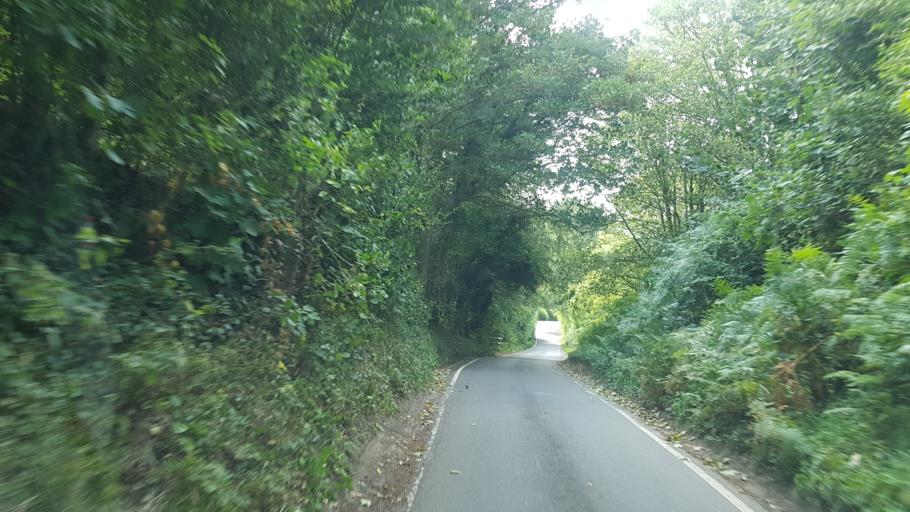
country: GB
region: England
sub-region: Kent
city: Harrietsham
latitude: 51.2463
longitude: 0.6372
